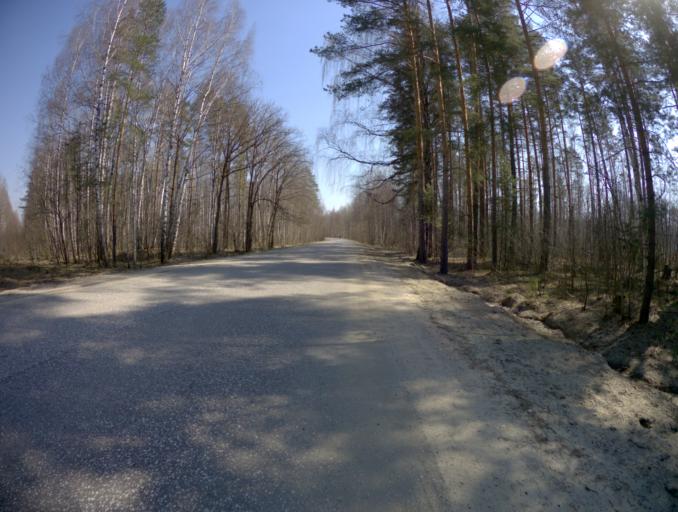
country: RU
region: Vladimir
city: Orgtrud
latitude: 56.1521
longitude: 40.5775
